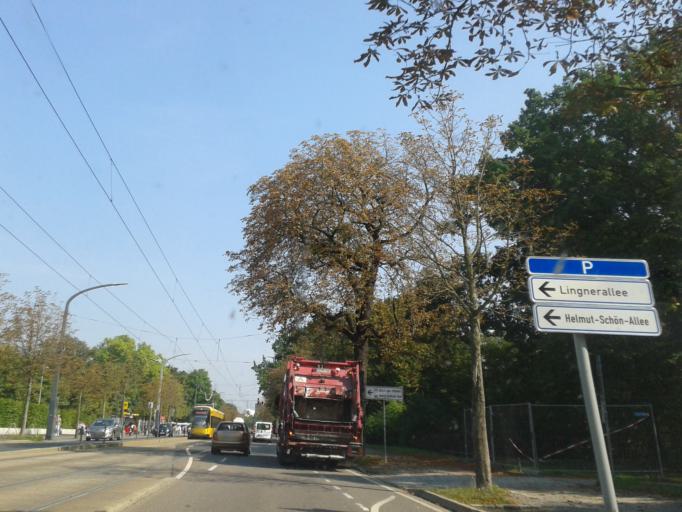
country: DE
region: Saxony
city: Dresden
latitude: 51.0412
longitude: 13.7501
